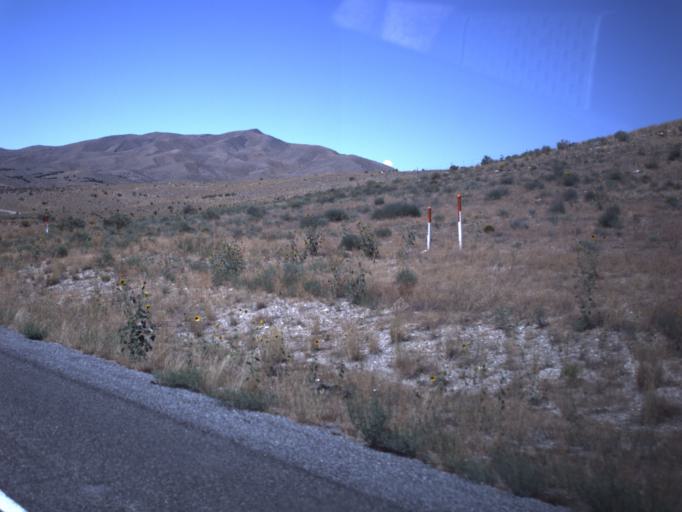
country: US
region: Utah
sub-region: Juab County
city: Nephi
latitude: 39.6348
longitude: -112.1060
